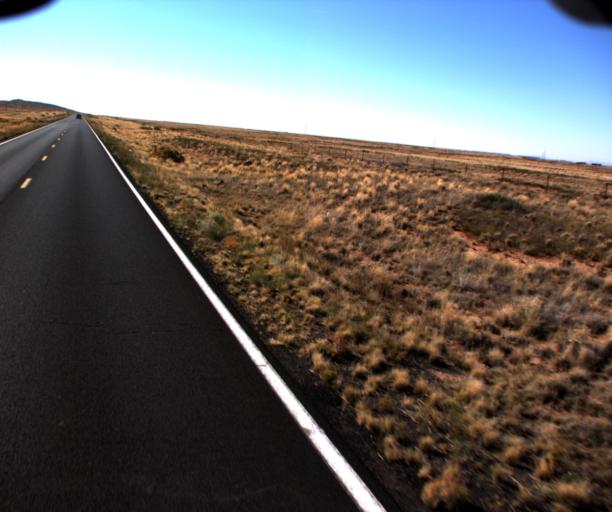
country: US
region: Arizona
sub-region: Navajo County
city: Dilkon
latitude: 35.3152
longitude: -110.4229
